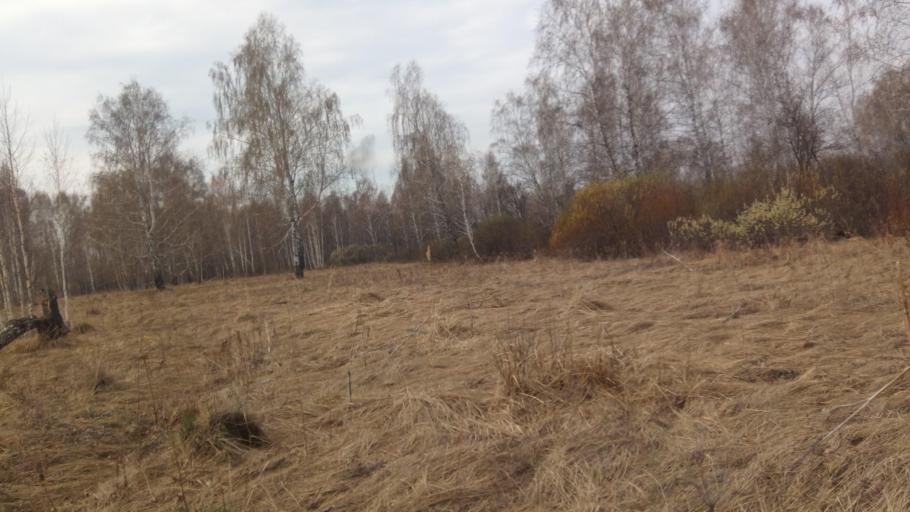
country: RU
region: Chelyabinsk
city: Timiryazevskiy
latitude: 54.9973
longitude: 60.8481
